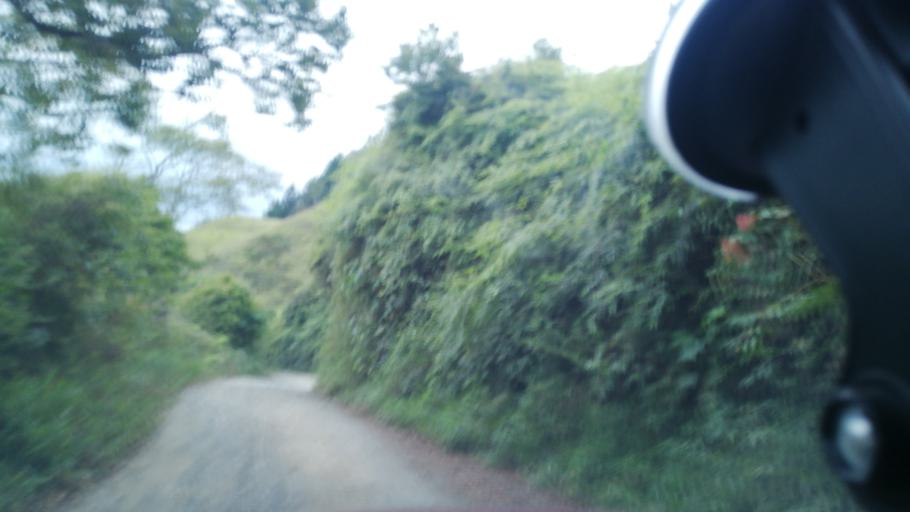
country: CO
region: Cundinamarca
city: Pacho
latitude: 5.1662
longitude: -74.2235
